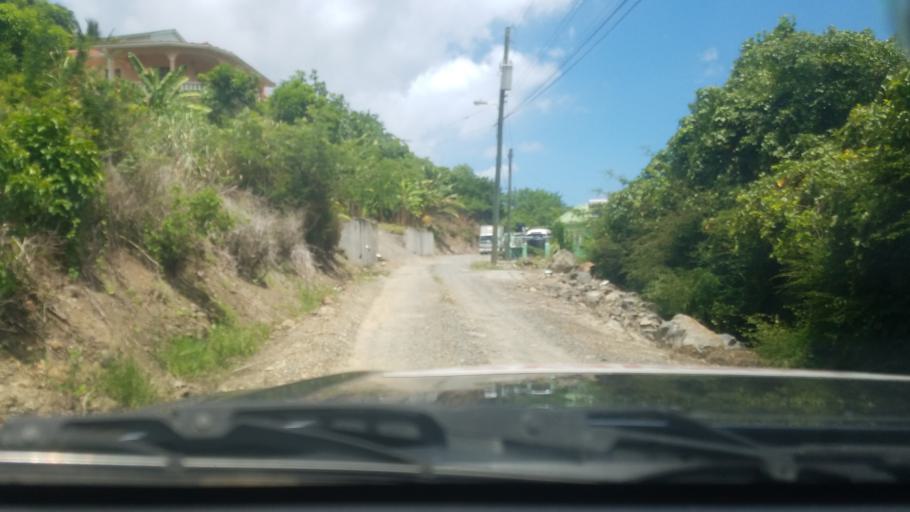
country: LC
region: Dennery Quarter
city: Dennery
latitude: 13.9183
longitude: -60.8961
